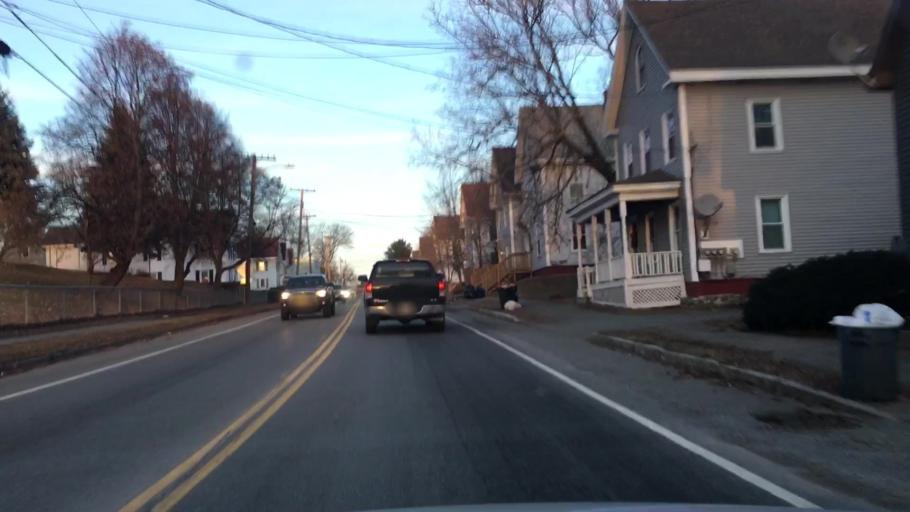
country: US
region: Maine
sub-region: Penobscot County
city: Brewer
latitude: 44.8034
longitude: -68.7588
